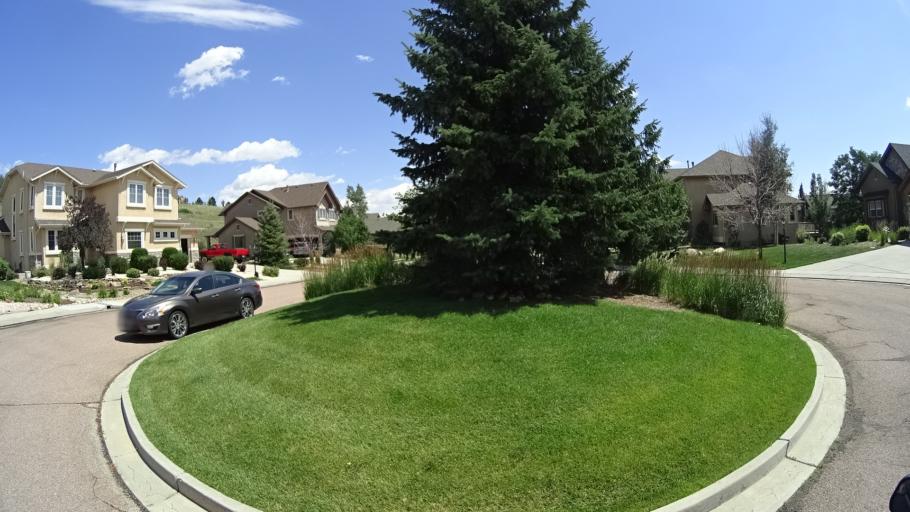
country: US
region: Colorado
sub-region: El Paso County
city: Black Forest
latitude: 38.9720
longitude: -104.7698
